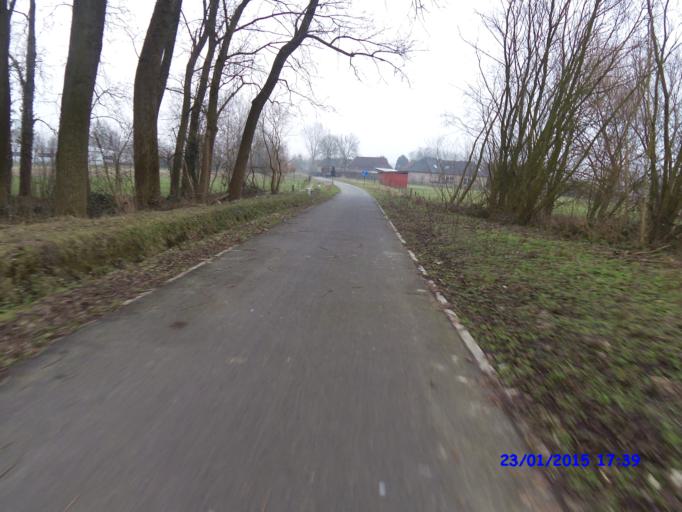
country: BE
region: Flanders
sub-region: Provincie Vlaams-Brabant
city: Opwijk
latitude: 50.9717
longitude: 4.1959
